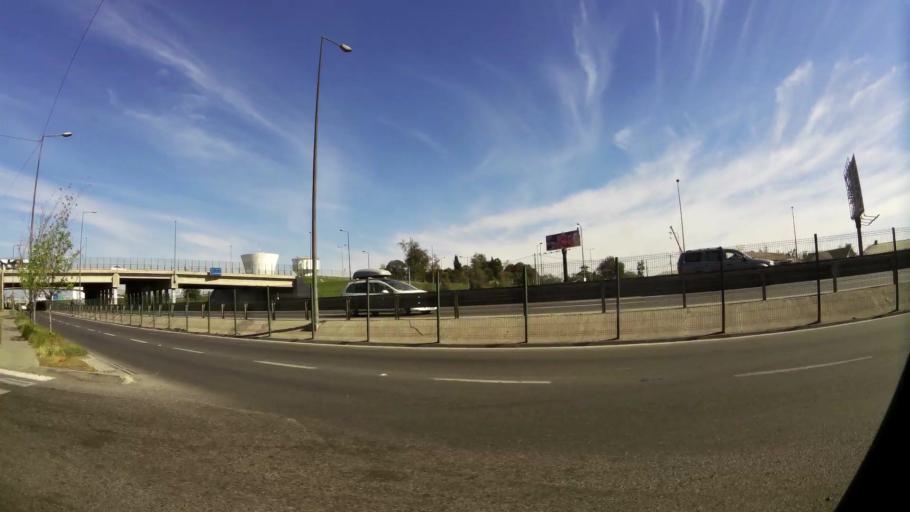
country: CL
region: Santiago Metropolitan
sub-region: Provincia de Santiago
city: Lo Prado
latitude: -33.5092
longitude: -70.7235
